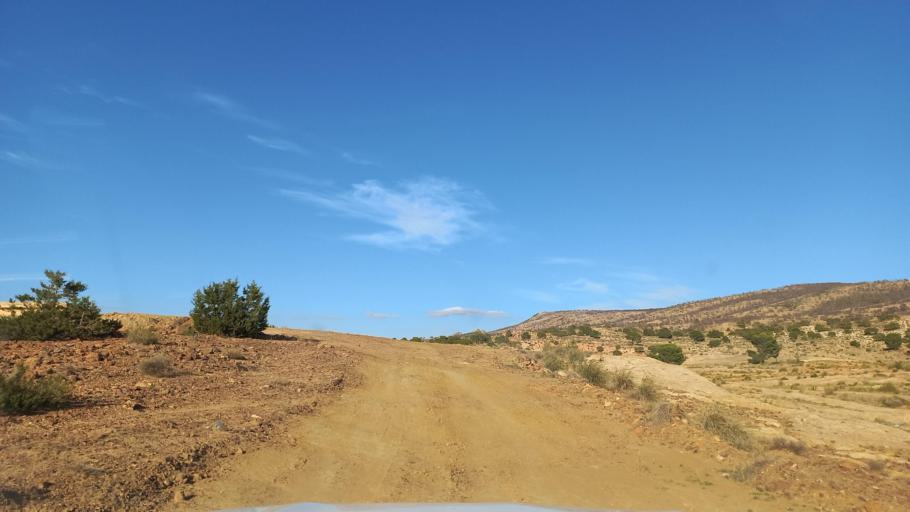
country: TN
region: Al Qasrayn
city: Sbiba
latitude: 35.3288
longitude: 9.1350
